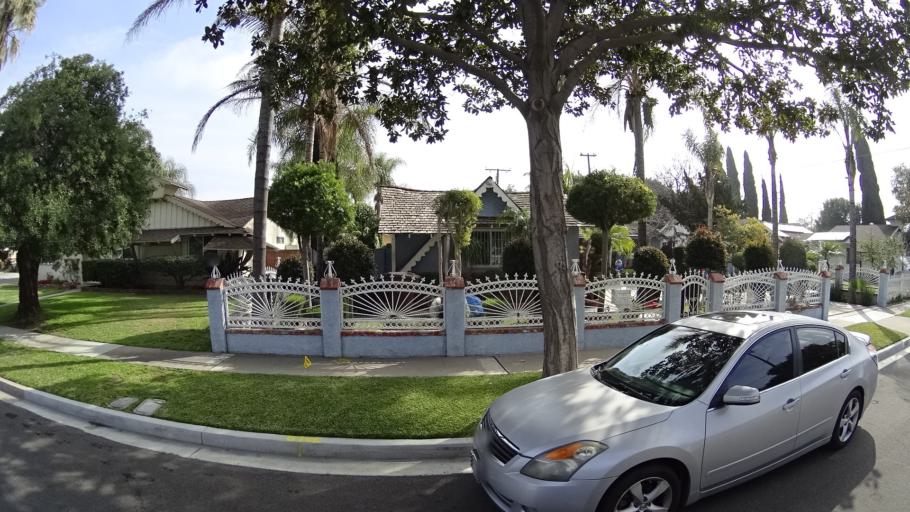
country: US
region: California
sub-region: Orange County
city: Stanton
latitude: 33.8116
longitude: -117.9725
